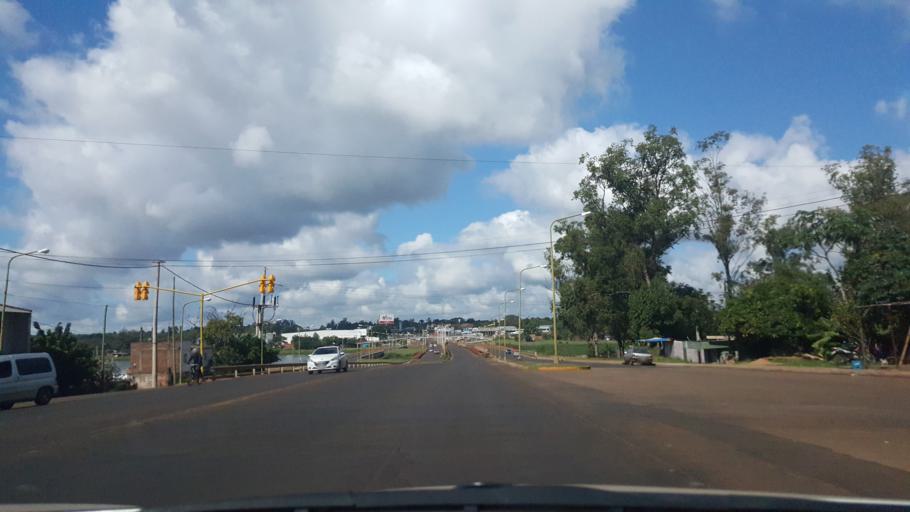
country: AR
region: Misiones
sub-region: Departamento de Capital
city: Posadas
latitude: -27.4161
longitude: -55.9000
